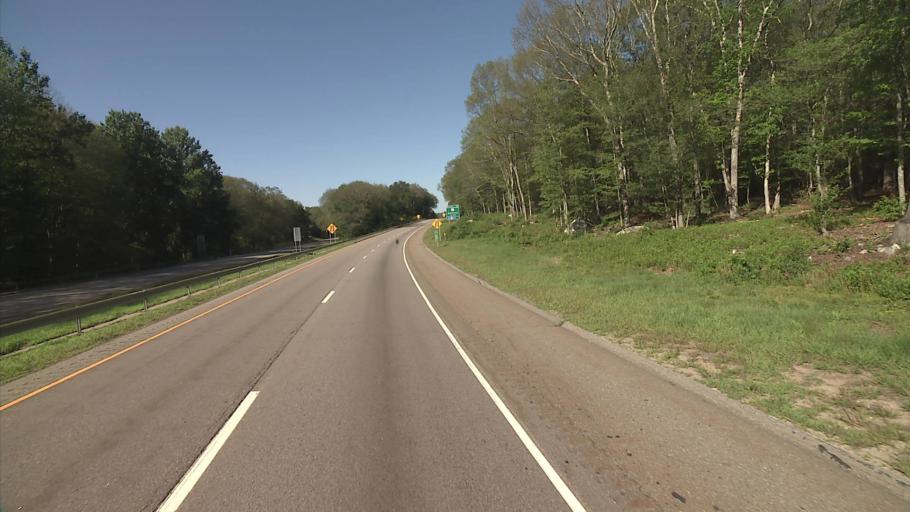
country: US
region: Connecticut
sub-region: New London County
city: Niantic
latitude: 41.3784
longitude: -72.1901
